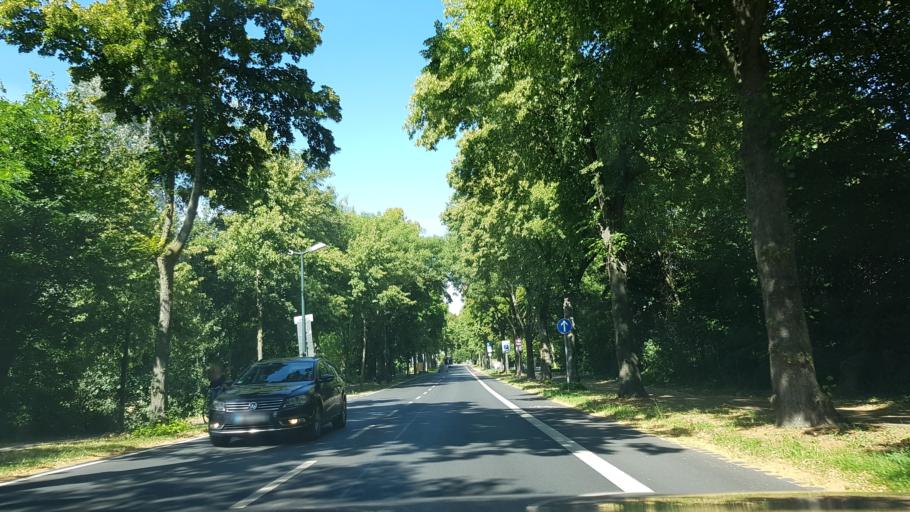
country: DE
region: North Rhine-Westphalia
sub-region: Regierungsbezirk Dusseldorf
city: Meerbusch
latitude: 51.2971
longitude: 6.7368
